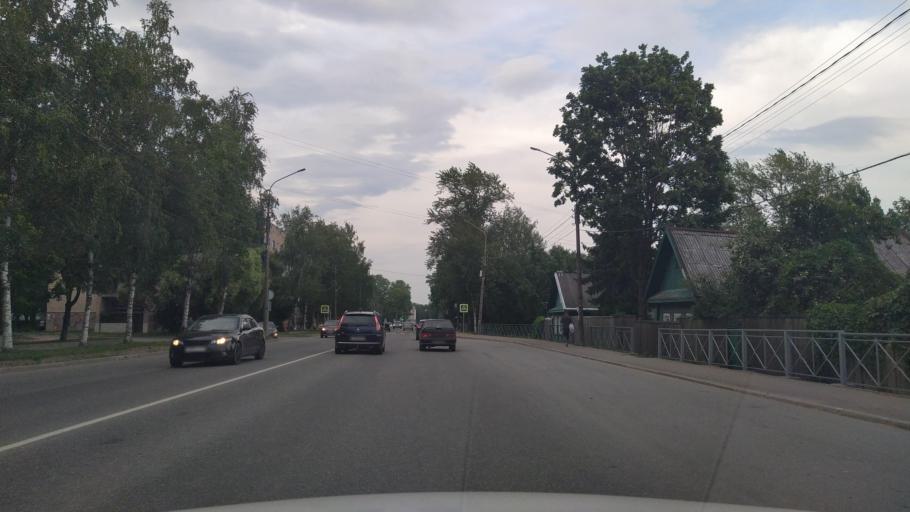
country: RU
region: Novgorod
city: Velikiy Novgorod
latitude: 58.5198
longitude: 31.2525
